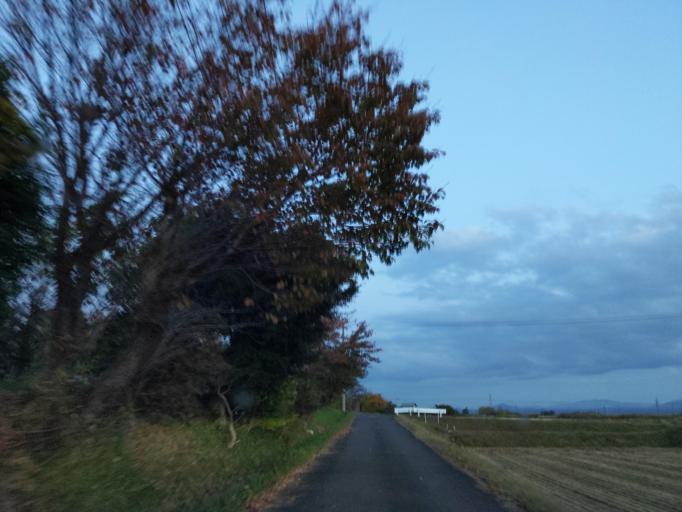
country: JP
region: Fukushima
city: Koriyama
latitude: 37.4629
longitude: 140.3192
